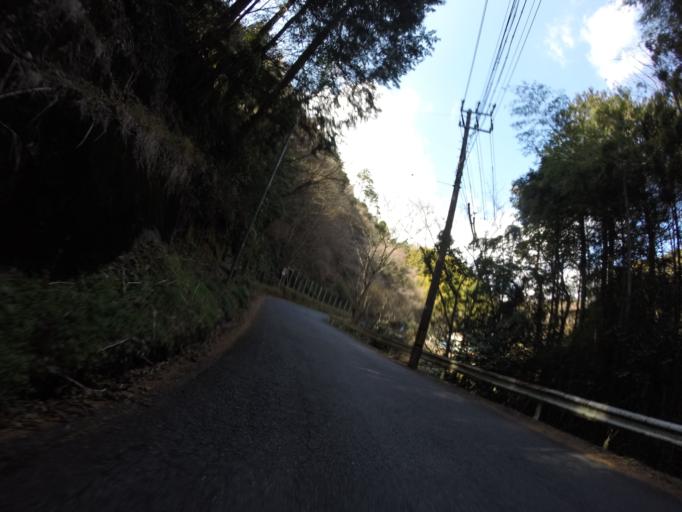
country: JP
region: Shizuoka
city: Shizuoka-shi
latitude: 35.0816
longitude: 138.4750
